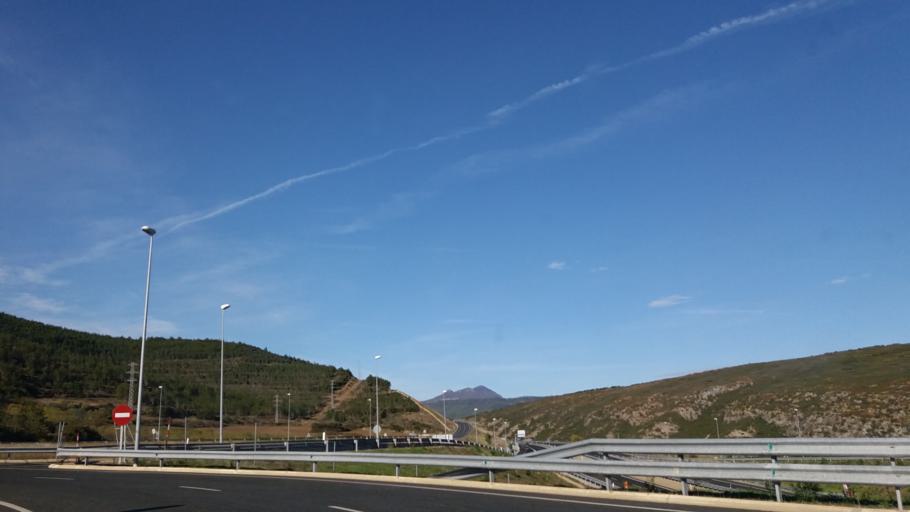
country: ES
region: Navarre
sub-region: Provincia de Navarra
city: Liedena
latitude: 42.6186
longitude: -1.3006
